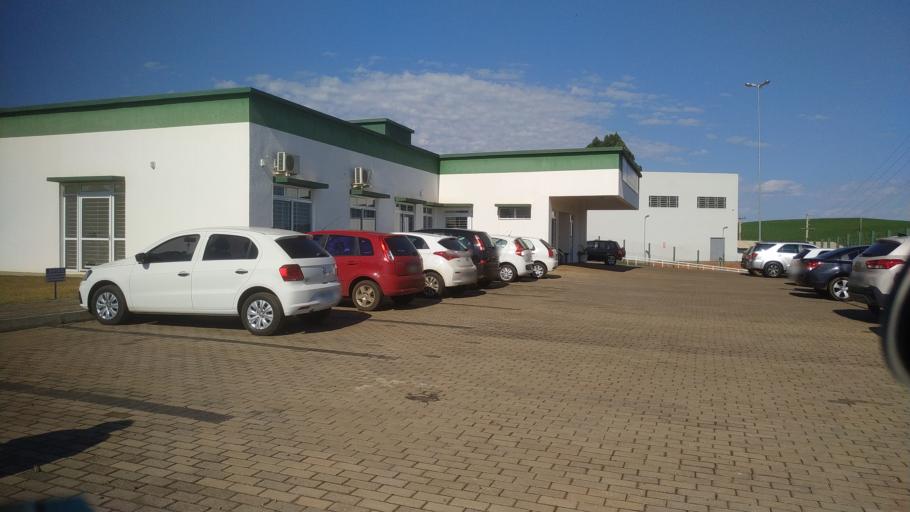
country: BR
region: Santa Catarina
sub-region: Chapeco
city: Chapeco
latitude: -27.0359
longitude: -52.6268
